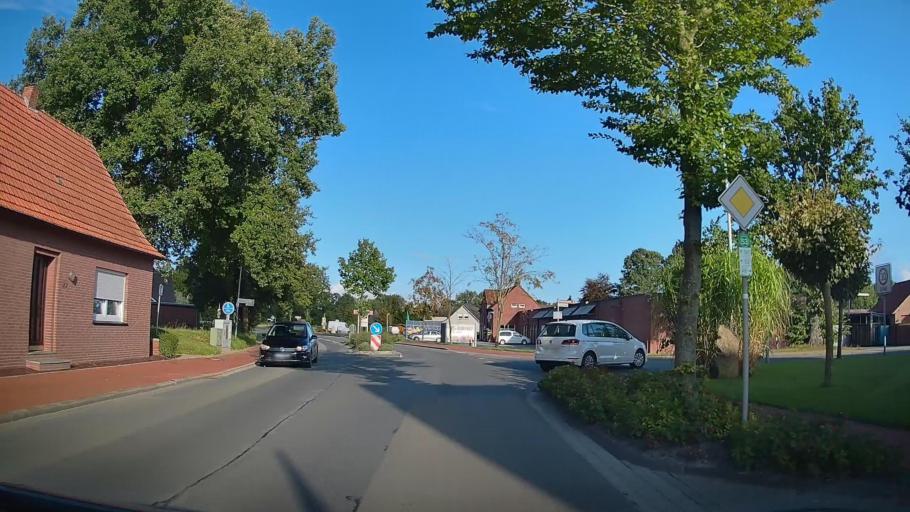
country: DE
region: Lower Saxony
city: Ostrhauderfehn
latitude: 53.1270
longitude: 7.6742
